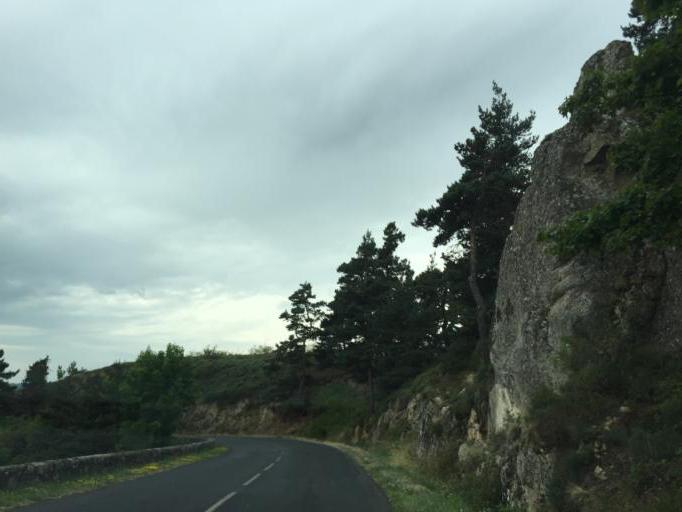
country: FR
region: Languedoc-Roussillon
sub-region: Departement de la Lozere
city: Langogne
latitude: 44.8224
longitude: 3.7842
